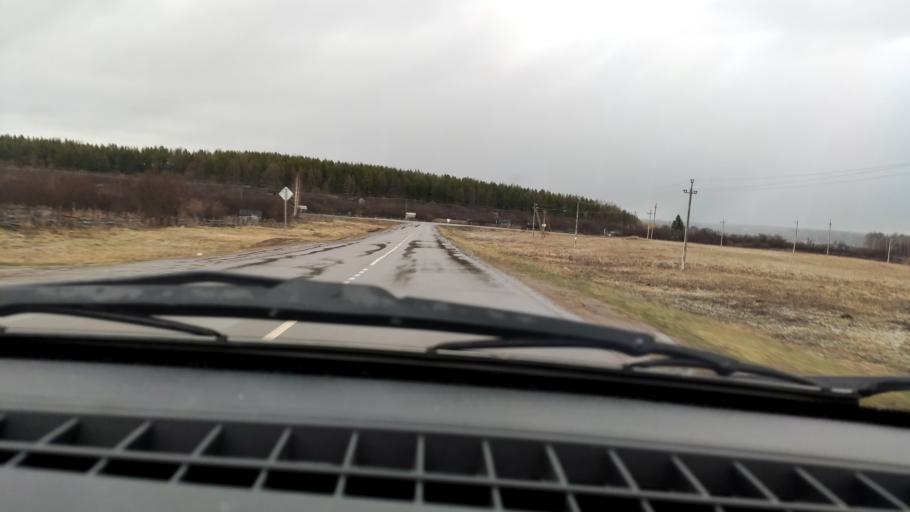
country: RU
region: Bashkortostan
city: Chekmagush
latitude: 55.1564
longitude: 54.6304
